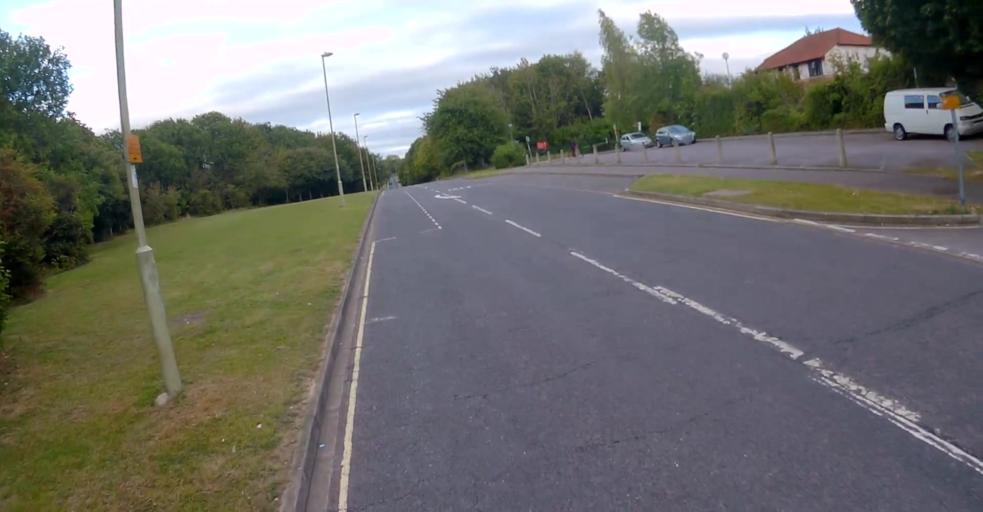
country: GB
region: England
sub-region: Hampshire
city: Basingstoke
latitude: 51.2403
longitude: -1.1235
